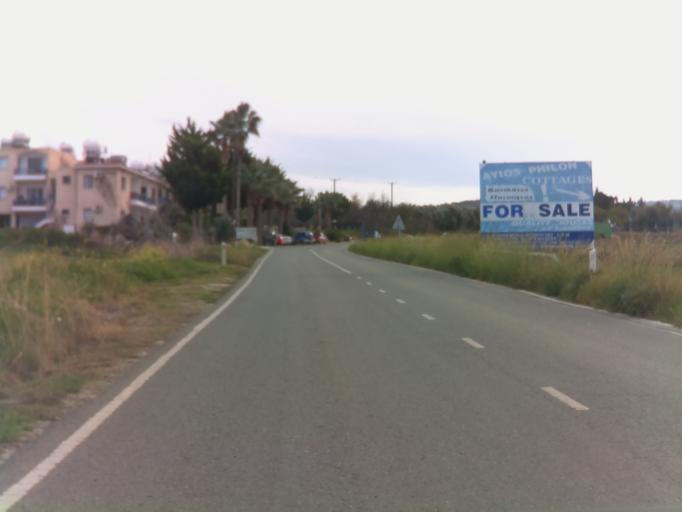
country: CY
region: Pafos
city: Polis
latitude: 35.0253
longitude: 32.4148
